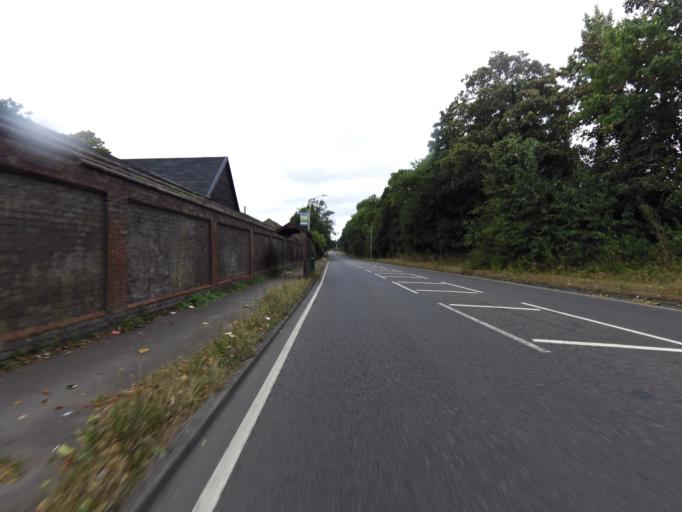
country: GB
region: England
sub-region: Hertfordshire
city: Radlett
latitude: 51.7078
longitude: -0.3304
